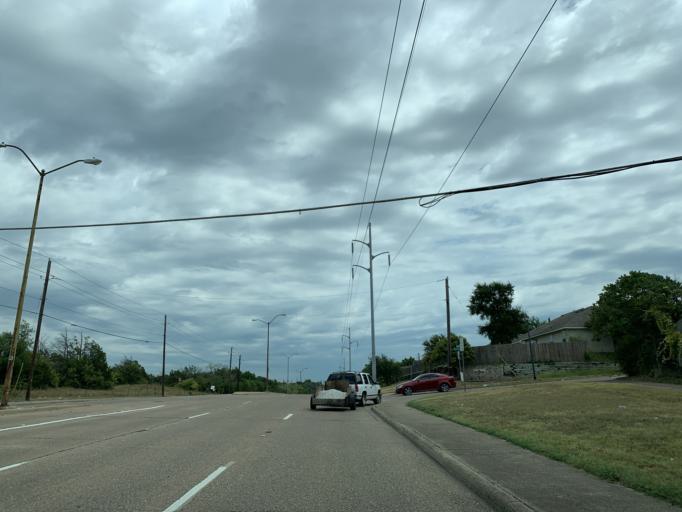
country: US
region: Texas
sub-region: Dallas County
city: DeSoto
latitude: 32.6623
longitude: -96.8127
